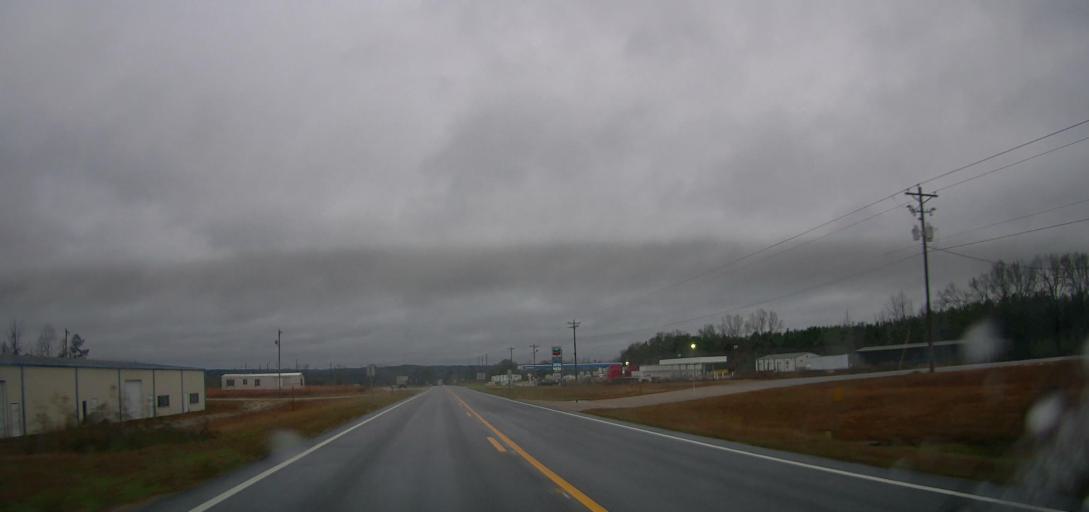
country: US
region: Alabama
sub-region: Chilton County
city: Thorsby
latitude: 32.7720
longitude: -86.8817
